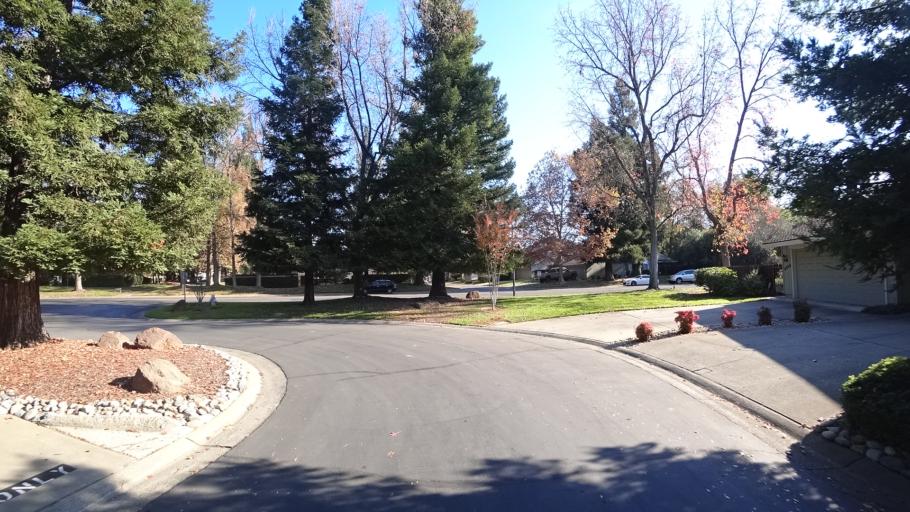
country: US
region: California
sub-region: Sacramento County
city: Citrus Heights
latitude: 38.6874
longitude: -121.3014
